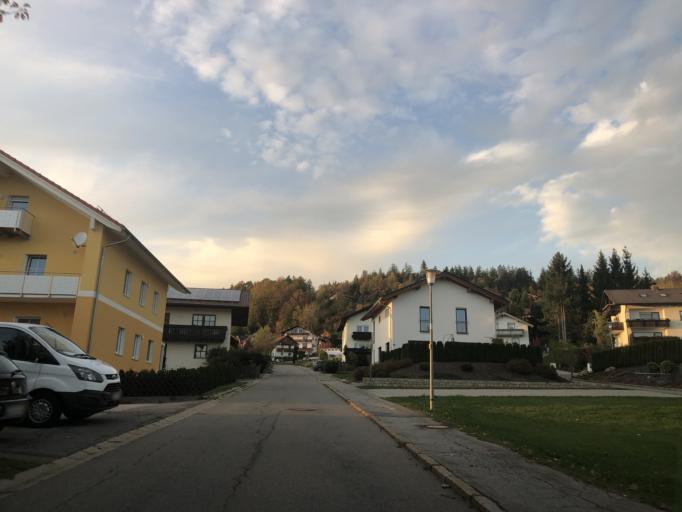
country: DE
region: Bavaria
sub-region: Lower Bavaria
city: Bodenmais
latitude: 49.0711
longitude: 13.0954
